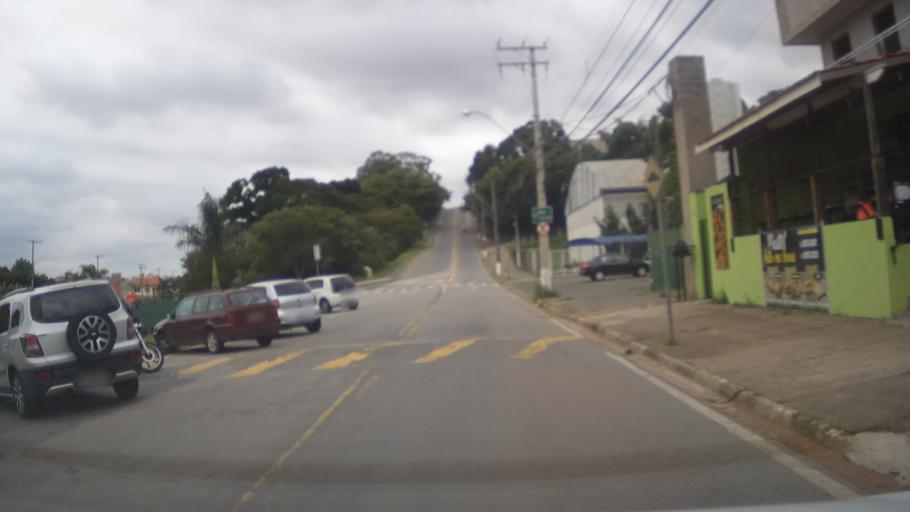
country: BR
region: Sao Paulo
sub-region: Vinhedo
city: Vinhedo
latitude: -23.0111
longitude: -46.9815
